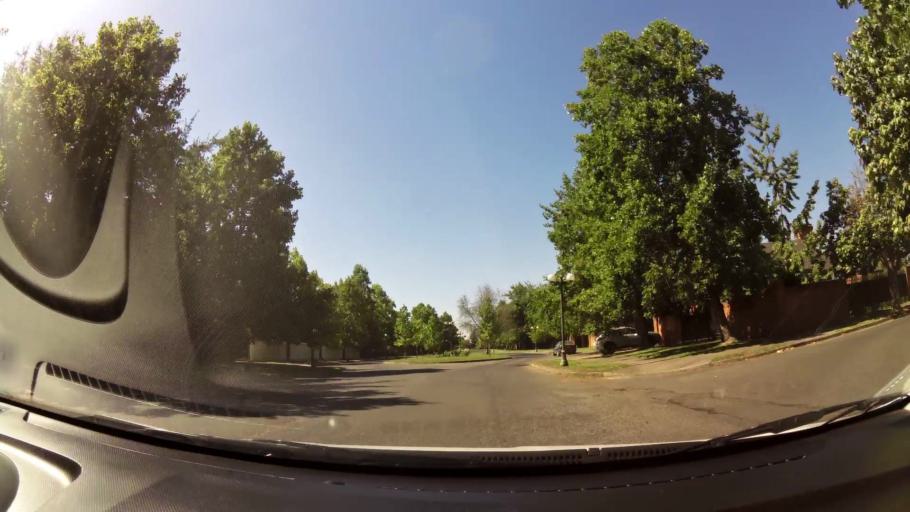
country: CL
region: Maule
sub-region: Provincia de Talca
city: Talca
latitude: -35.4343
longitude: -71.6156
